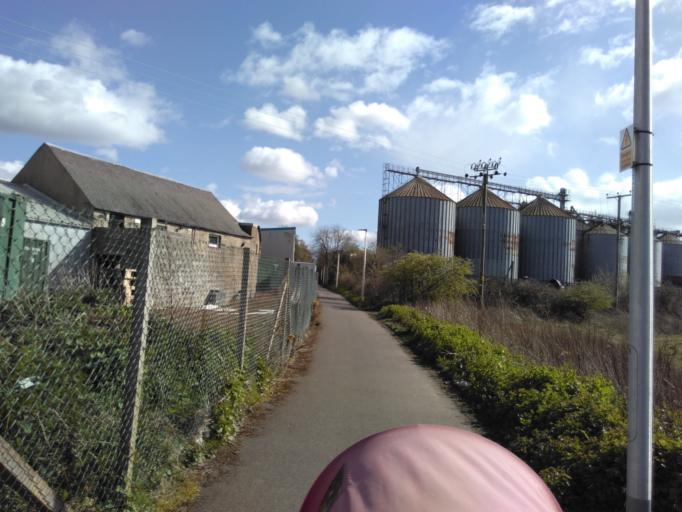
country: GB
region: Scotland
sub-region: Midlothian
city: Loanhead
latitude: 55.8865
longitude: -3.1473
